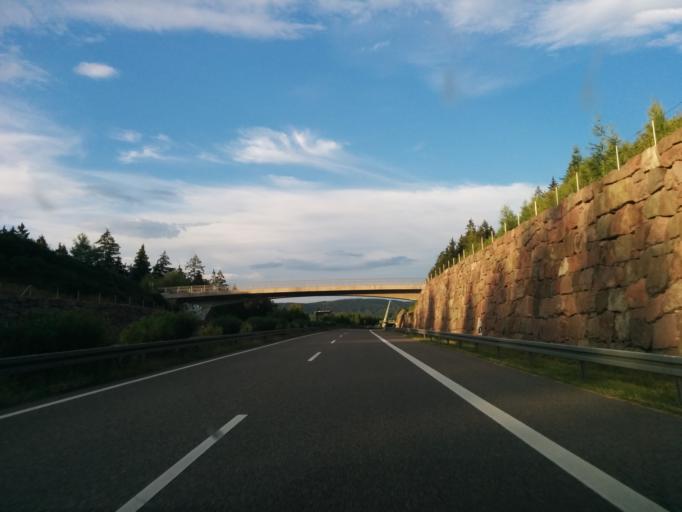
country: DE
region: Thuringia
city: Suhl
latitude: 50.5871
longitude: 10.6761
